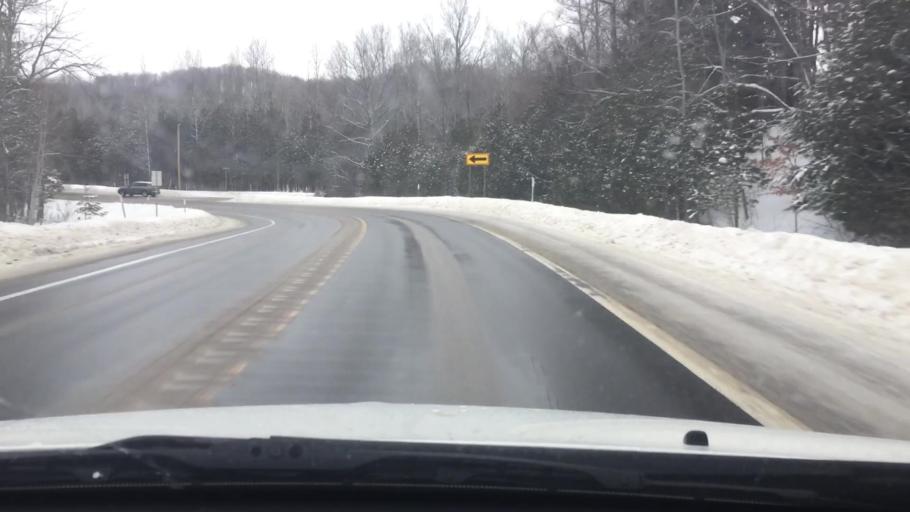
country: US
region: Michigan
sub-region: Charlevoix County
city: East Jordan
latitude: 45.1315
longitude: -85.0813
